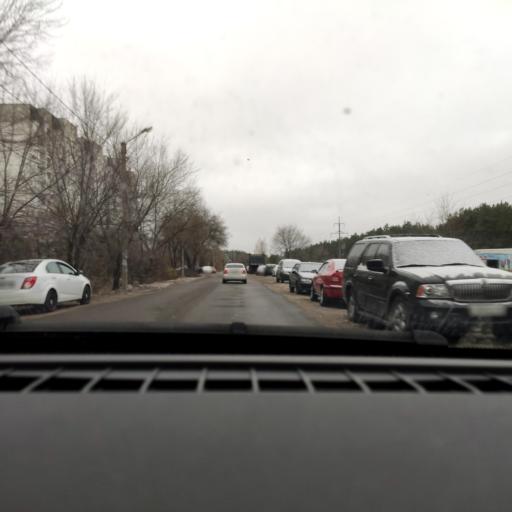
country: RU
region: Voronezj
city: Somovo
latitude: 51.7357
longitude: 39.2963
